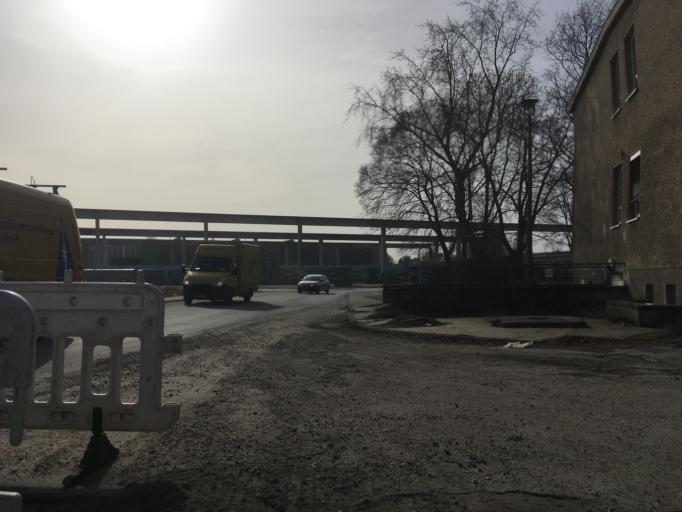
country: DE
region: Berlin
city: Kopenick Bezirk
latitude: 52.4310
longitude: 13.5687
